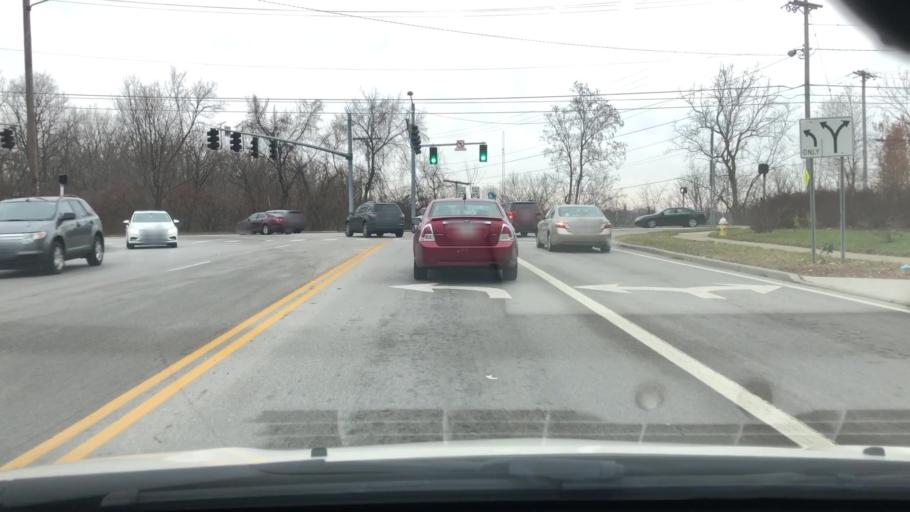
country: US
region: Ohio
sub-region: Wood County
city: Perrysburg
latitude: 41.5549
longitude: -83.6410
